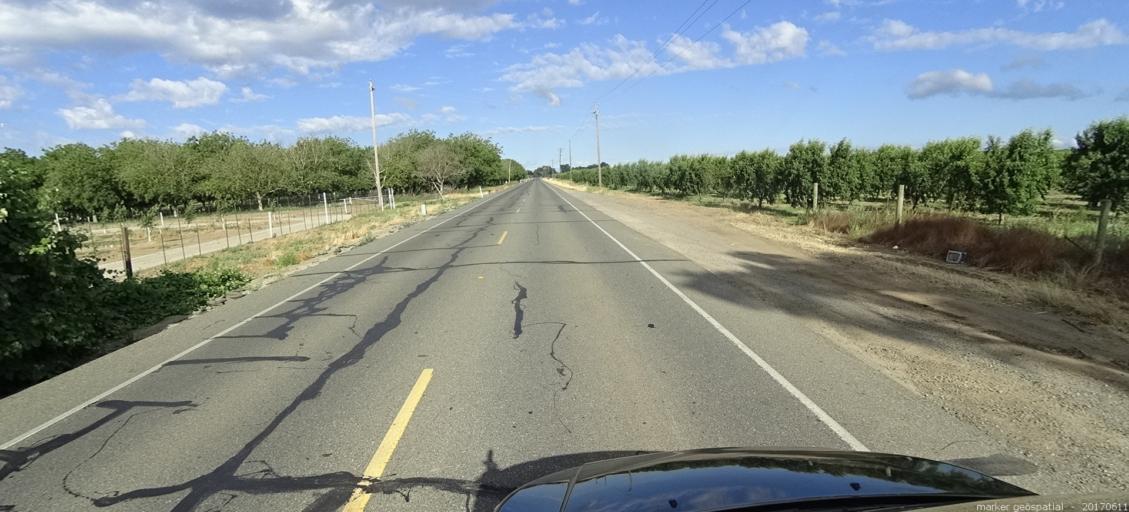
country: US
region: California
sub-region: Butte County
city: Gridley
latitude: 39.3643
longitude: -121.6267
